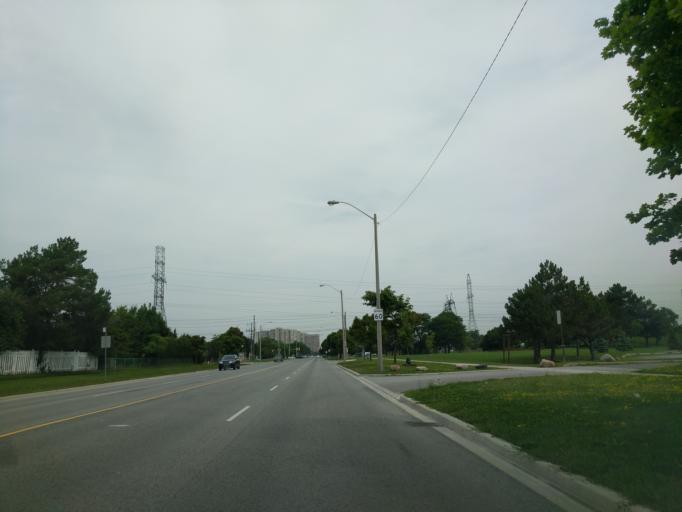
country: CA
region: Ontario
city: Scarborough
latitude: 43.8037
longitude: -79.3197
